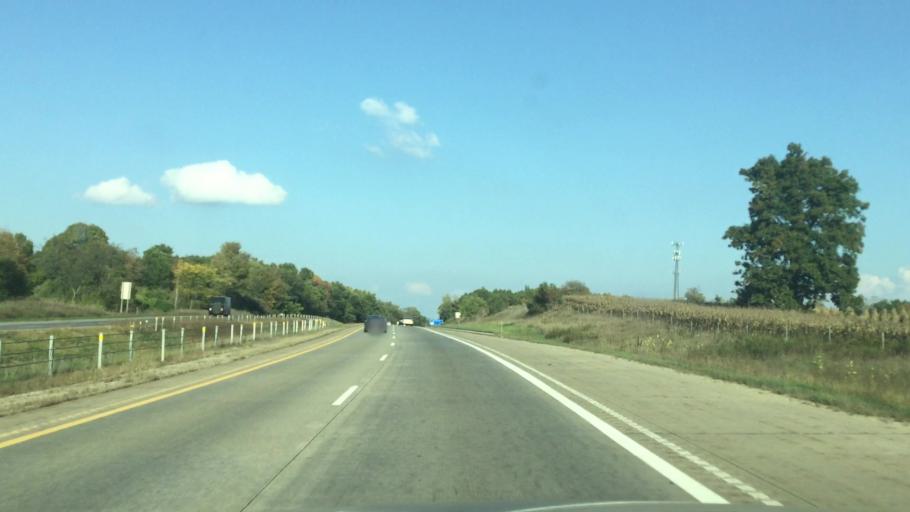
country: US
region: Michigan
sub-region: Jackson County
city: Grass Lake
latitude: 42.2933
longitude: -84.1584
